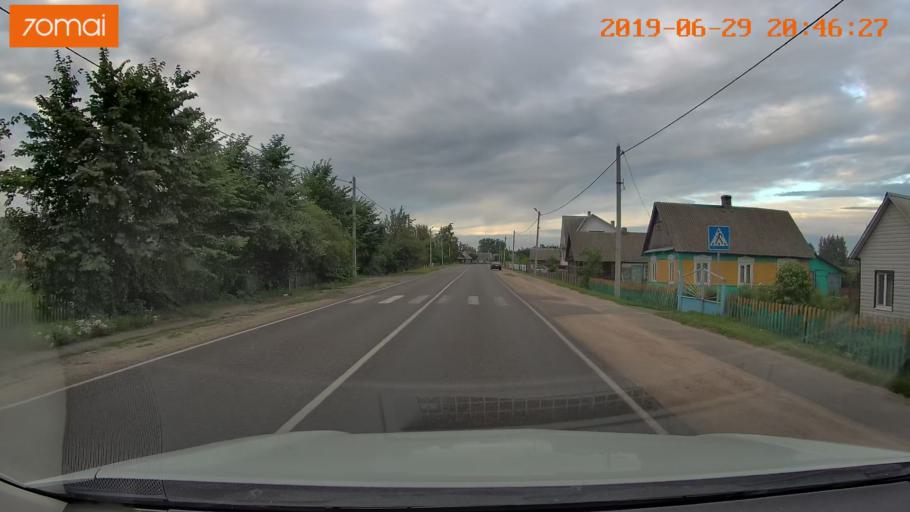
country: BY
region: Brest
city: Hantsavichy
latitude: 52.6309
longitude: 26.3086
